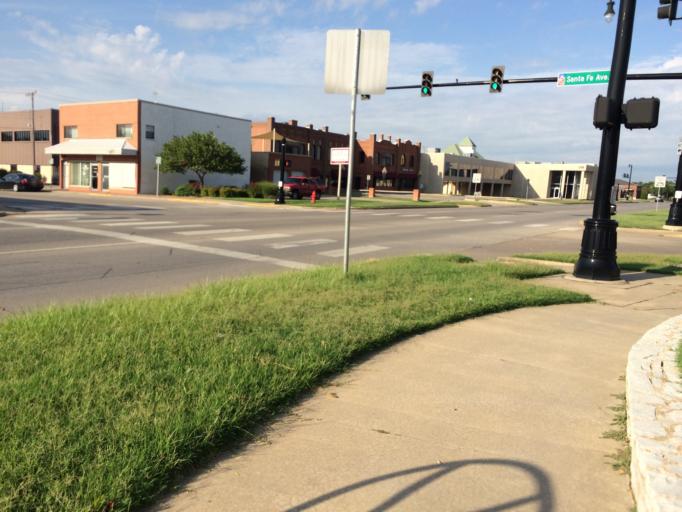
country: US
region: Oklahoma
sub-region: Cleveland County
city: Norman
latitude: 35.2212
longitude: -97.4458
